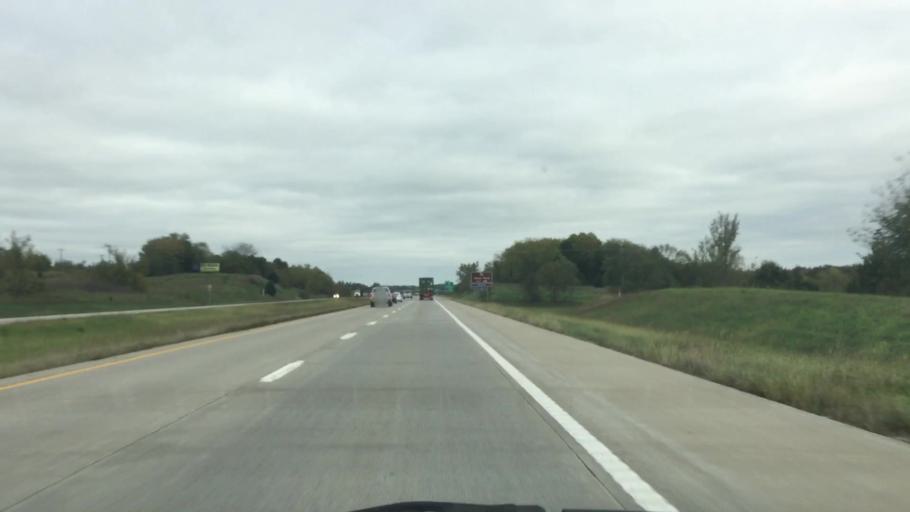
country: US
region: Missouri
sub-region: Clinton County
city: Cameron
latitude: 39.6601
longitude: -94.2375
